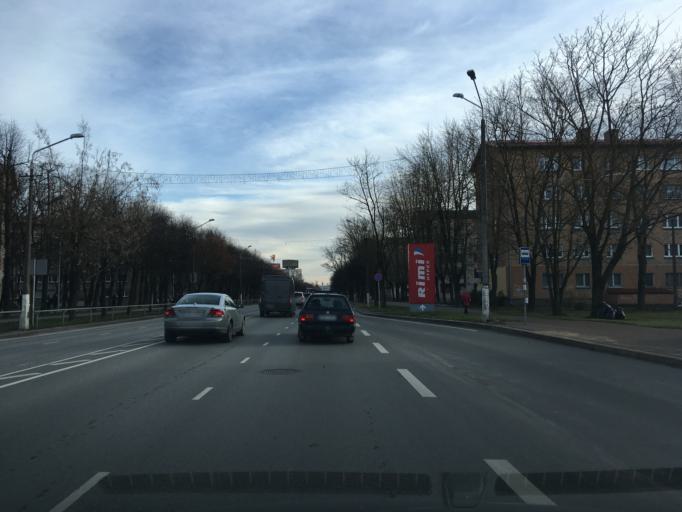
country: EE
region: Ida-Virumaa
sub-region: Narva linn
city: Narva
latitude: 59.3793
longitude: 28.1805
